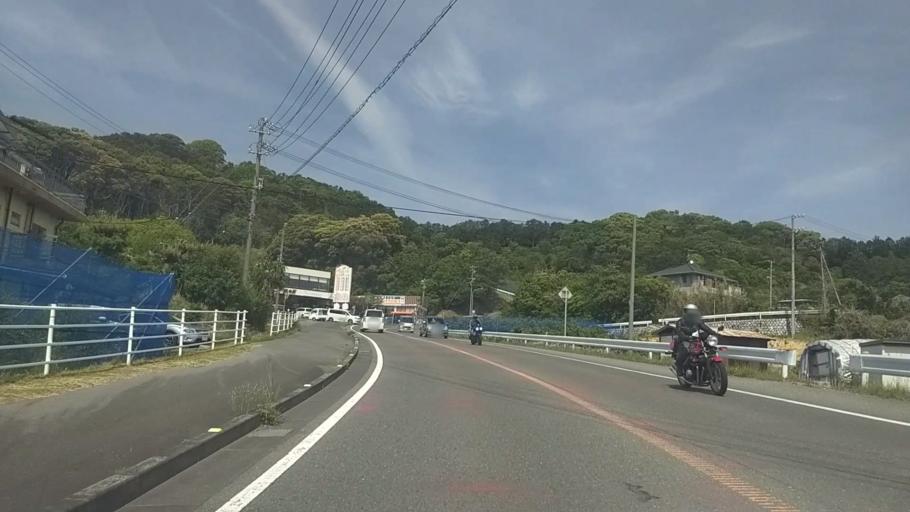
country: JP
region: Shizuoka
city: Kosai-shi
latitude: 34.7883
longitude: 137.6062
